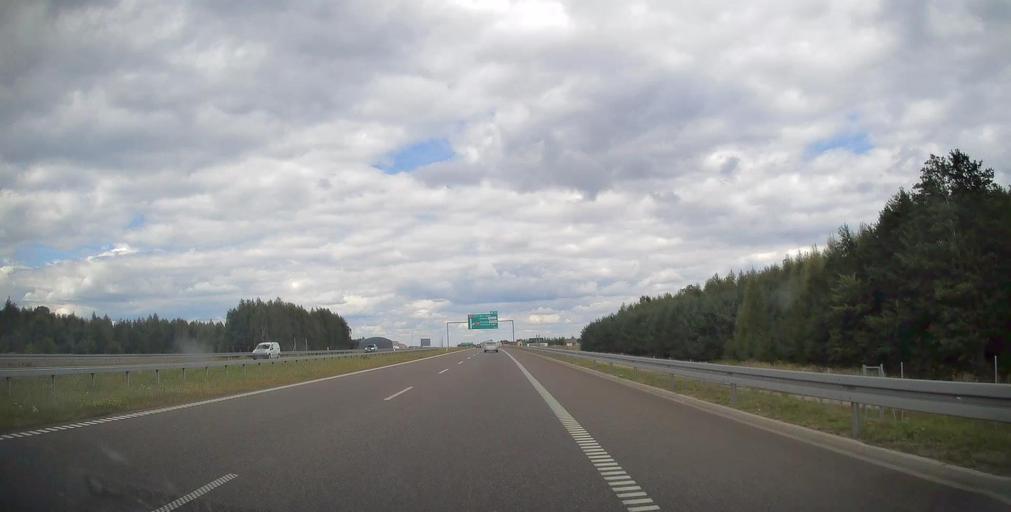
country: PL
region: Masovian Voivodeship
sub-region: Powiat radomski
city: Wolanow
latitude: 51.3783
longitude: 21.0192
